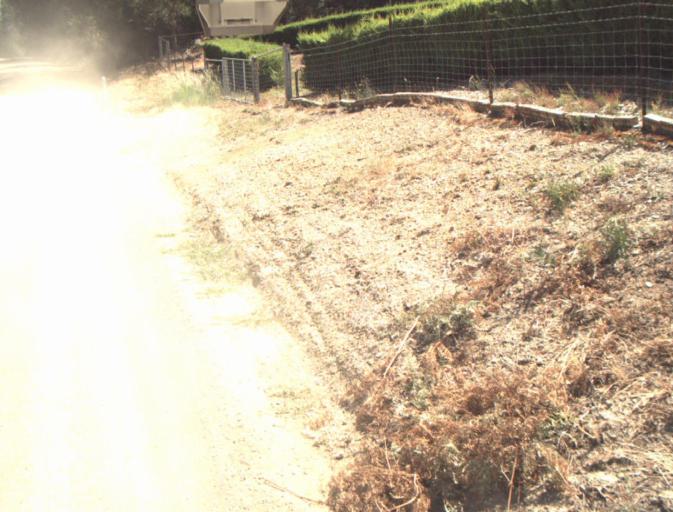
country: AU
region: Tasmania
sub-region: Launceston
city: Mayfield
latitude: -41.2576
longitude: 147.1877
